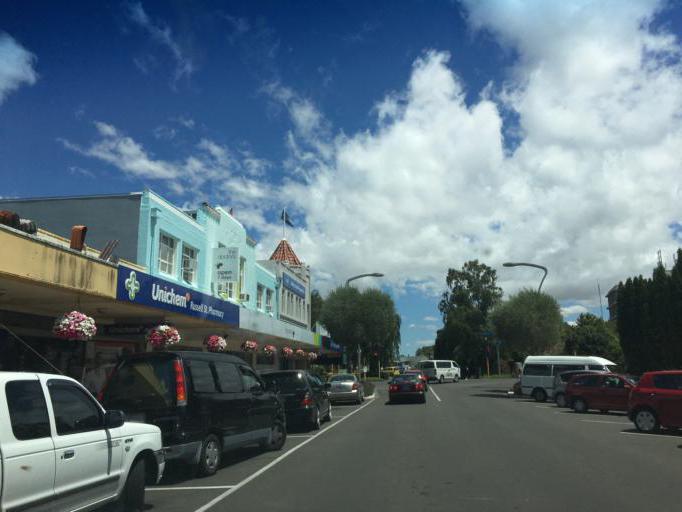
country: NZ
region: Hawke's Bay
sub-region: Hastings District
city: Hastings
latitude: -39.6424
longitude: 176.8429
